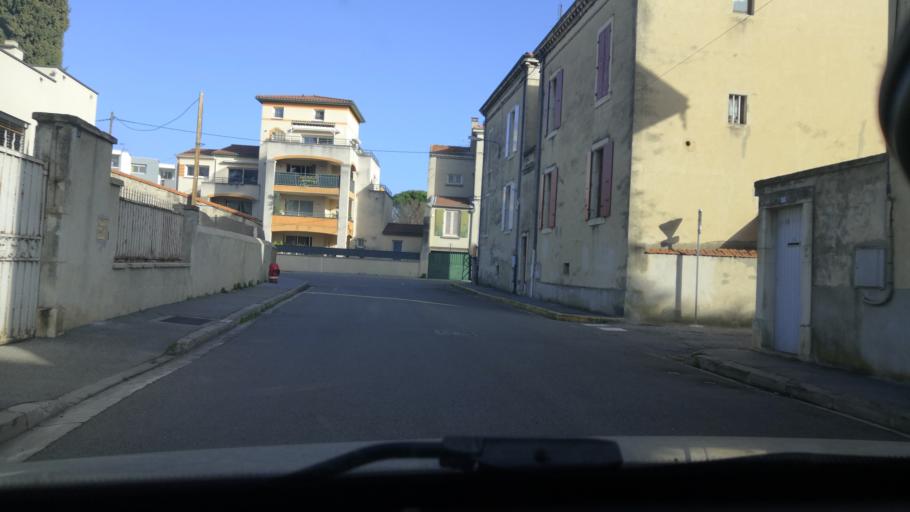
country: FR
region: Rhone-Alpes
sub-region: Departement de la Drome
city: Montelimar
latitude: 44.5572
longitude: 4.7410
